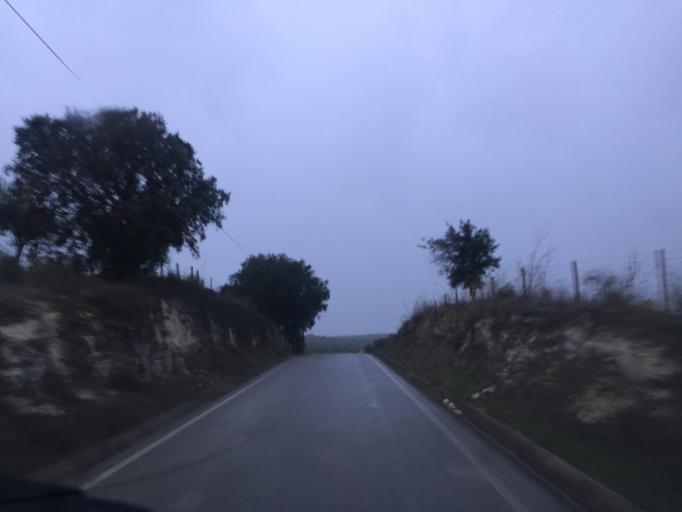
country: PT
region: Portalegre
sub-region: Avis
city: Avis
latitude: 39.0410
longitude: -7.9123
